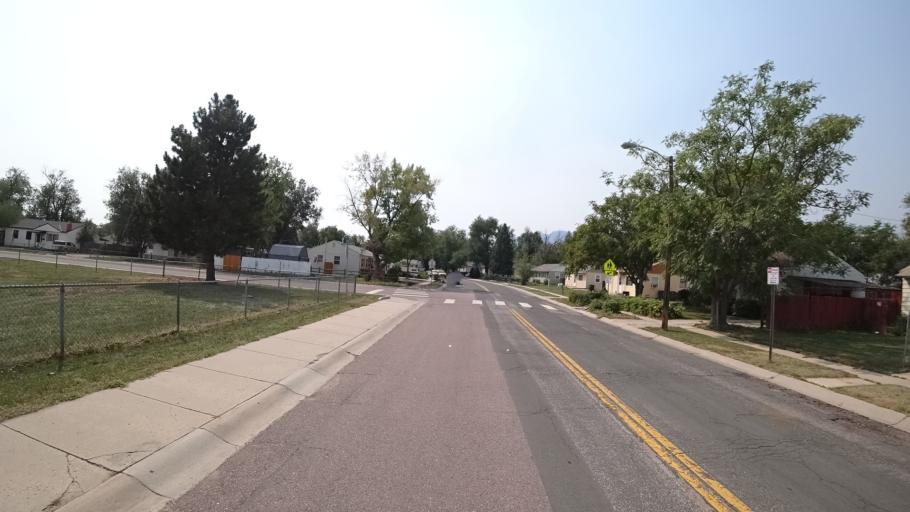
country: US
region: Colorado
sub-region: El Paso County
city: Colorado Springs
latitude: 38.8054
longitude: -104.8138
